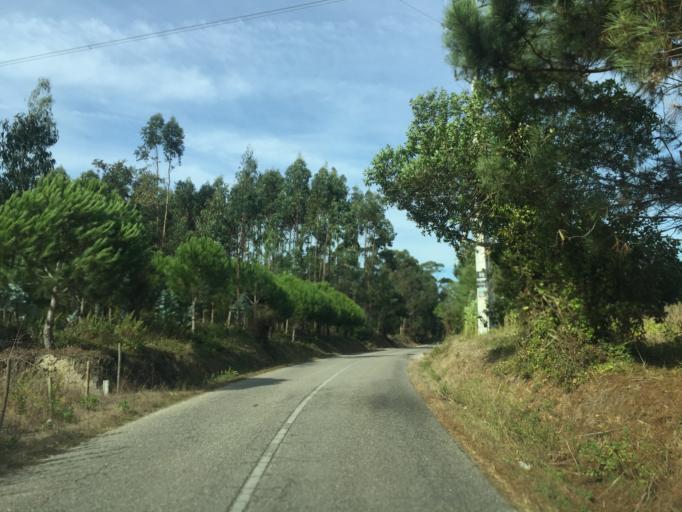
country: PT
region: Coimbra
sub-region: Figueira da Foz
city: Lavos
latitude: 40.0757
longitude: -8.8222
